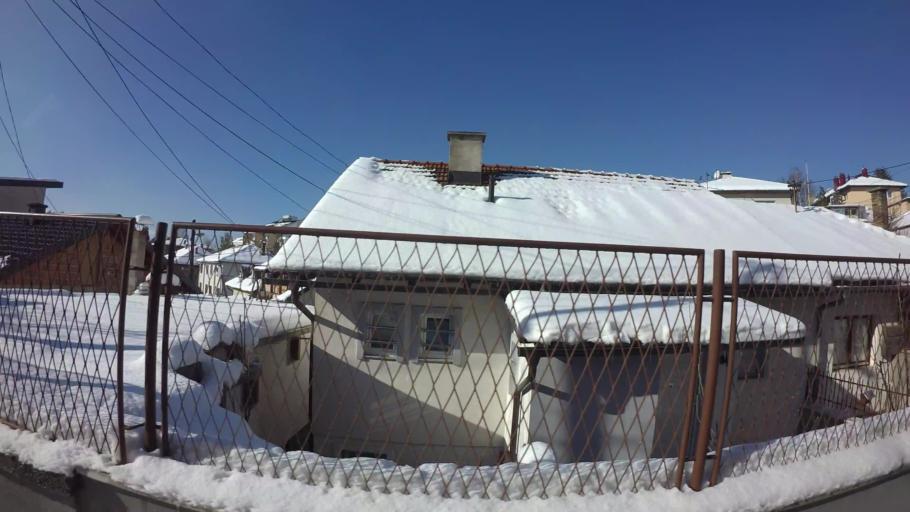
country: BA
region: Federation of Bosnia and Herzegovina
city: Kobilja Glava
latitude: 43.8646
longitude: 18.4212
